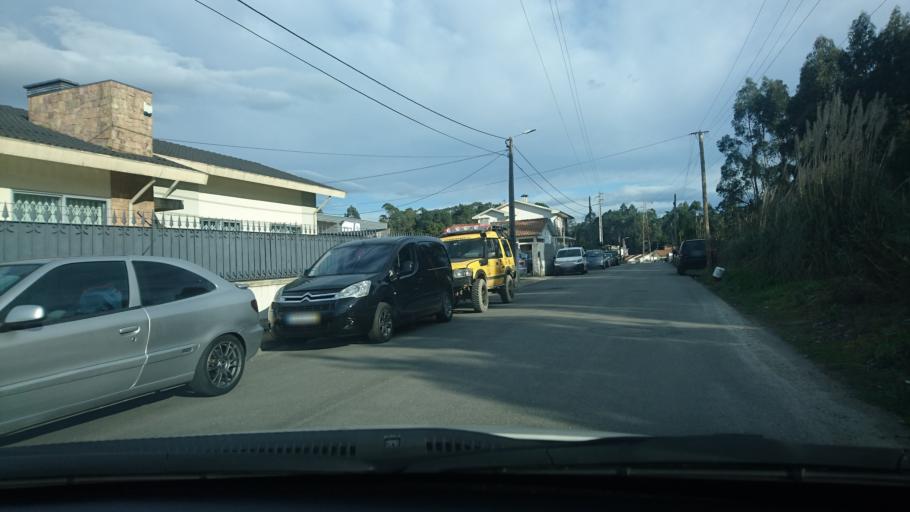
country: PT
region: Aveiro
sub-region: Ovar
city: Cortegaca
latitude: 40.9581
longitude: -8.6027
